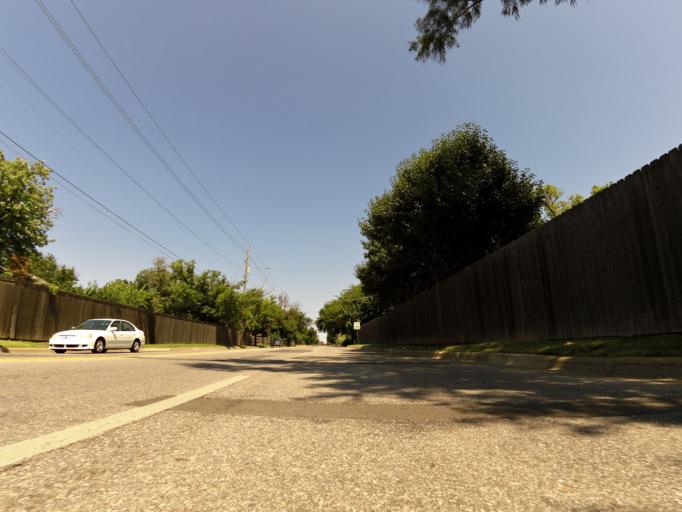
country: US
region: Kansas
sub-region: Sedgwick County
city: Wichita
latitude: 37.6867
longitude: -97.2621
